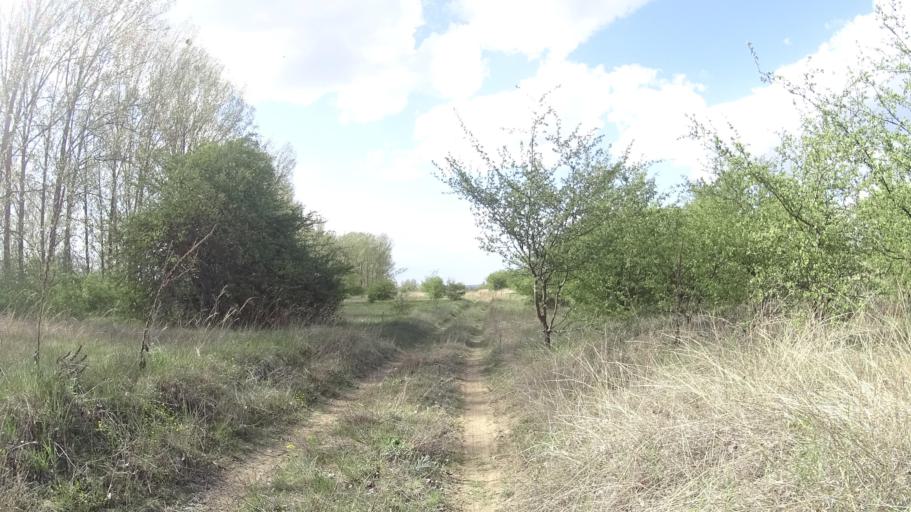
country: HU
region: Pest
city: Veresegyhaz
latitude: 47.6210
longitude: 19.2933
